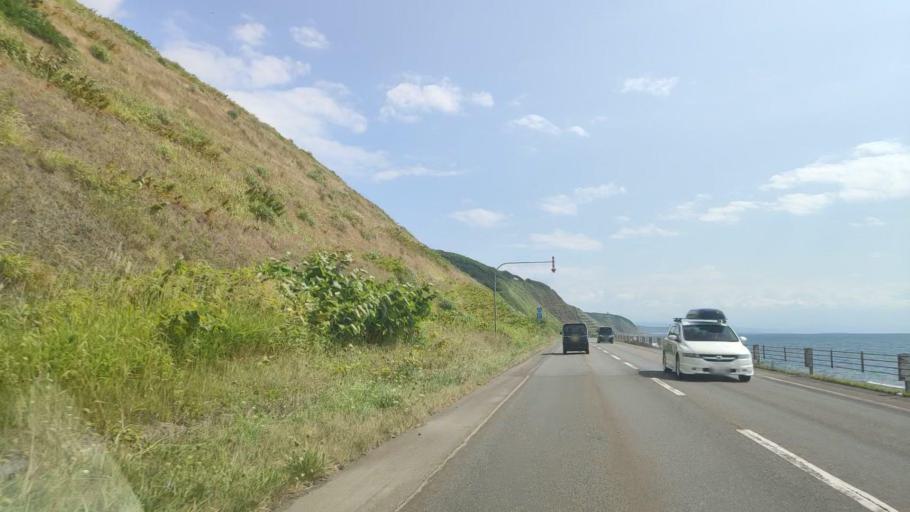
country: JP
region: Hokkaido
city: Rumoi
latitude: 44.0554
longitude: 141.6634
